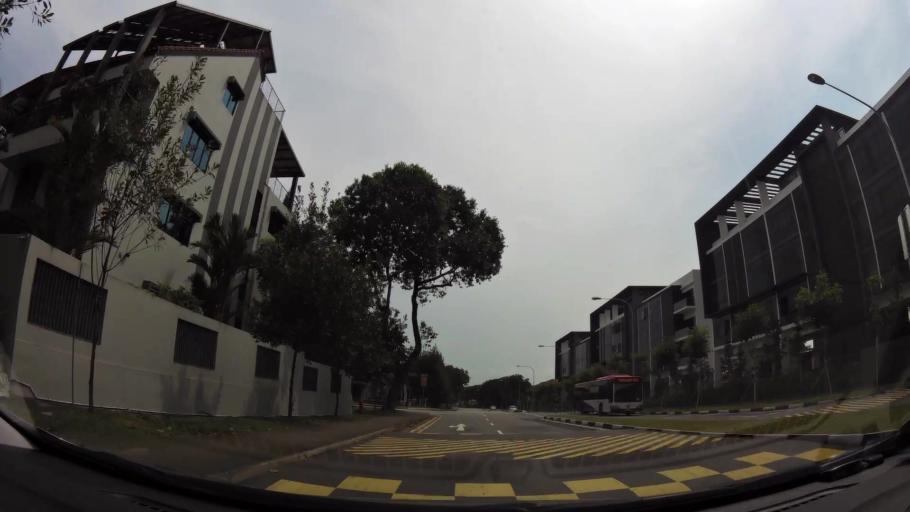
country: MY
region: Johor
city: Kampung Pasir Gudang Baru
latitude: 1.3803
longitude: 103.9436
